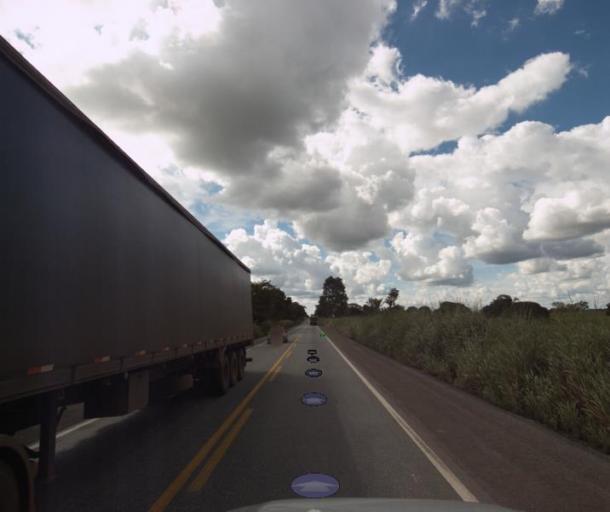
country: BR
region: Goias
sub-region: Porangatu
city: Porangatu
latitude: -13.2957
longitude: -49.1230
